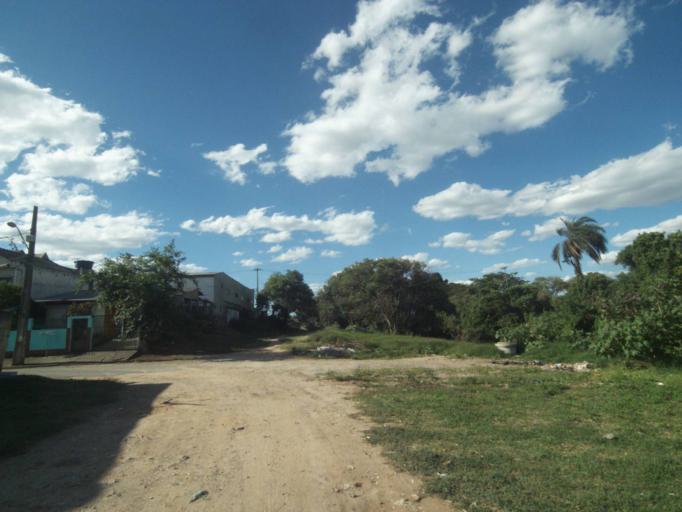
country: BR
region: Parana
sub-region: Curitiba
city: Curitiba
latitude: -25.4953
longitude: -49.3365
